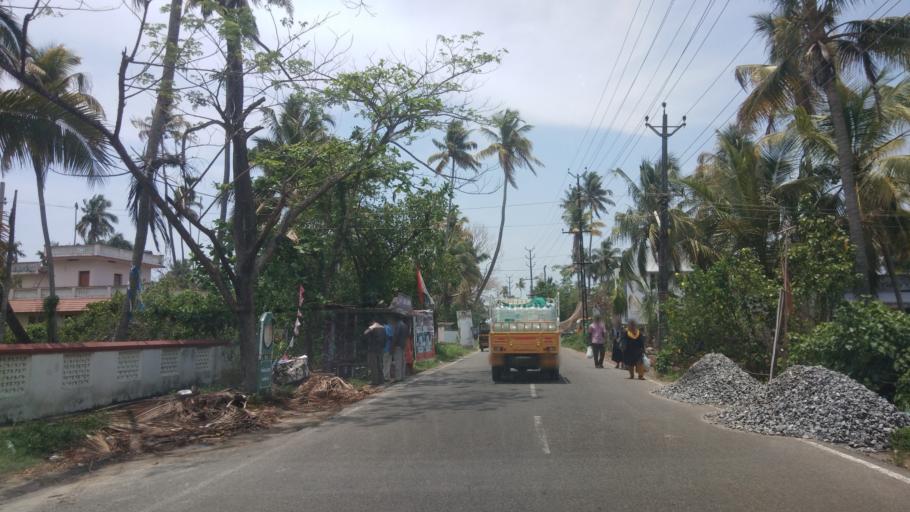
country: IN
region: Kerala
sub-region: Alappuzha
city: Kutiatodu
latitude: 9.8469
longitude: 76.2677
